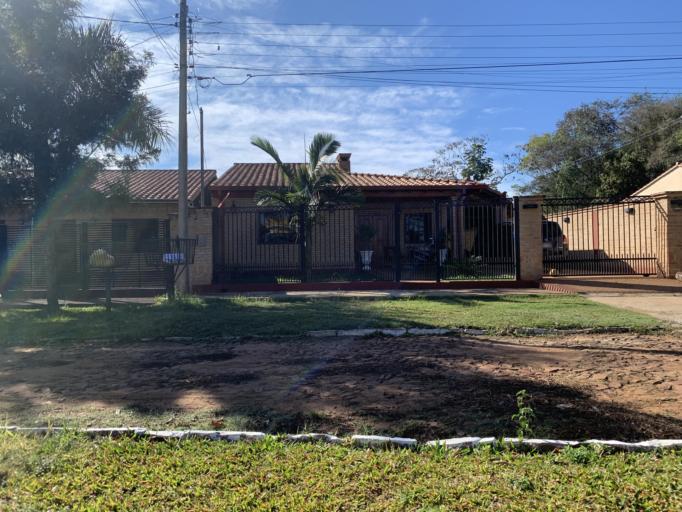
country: PY
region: Misiones
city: San Juan Bautista
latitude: -26.6647
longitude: -57.1357
